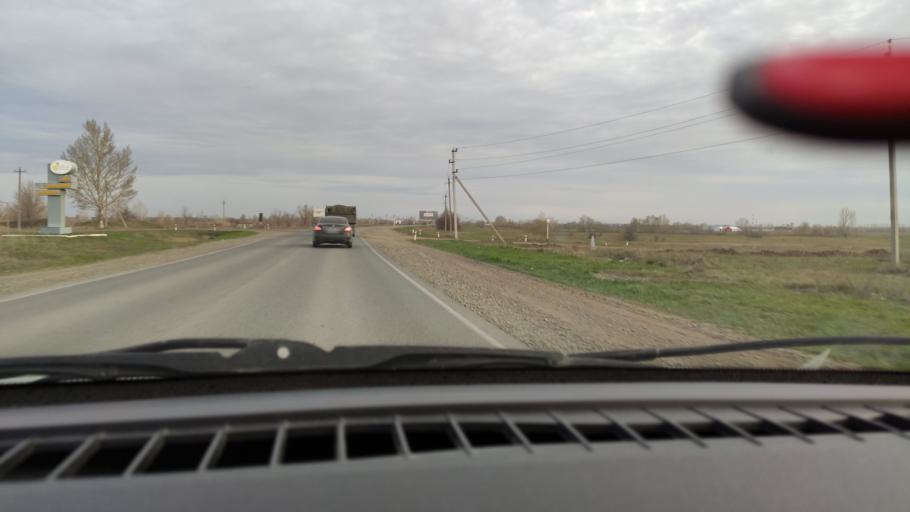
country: RU
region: Orenburg
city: Tatarskaya Kargala
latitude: 51.9128
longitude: 55.1736
